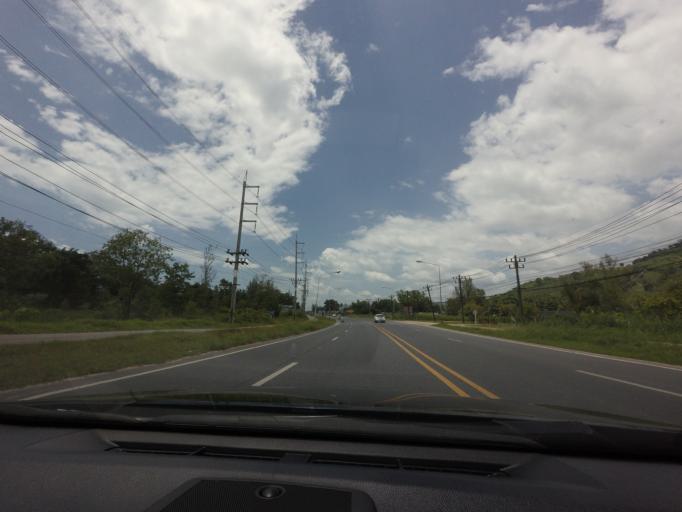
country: TH
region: Phangnga
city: Ban Khao Lak
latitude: 8.6535
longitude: 98.2534
